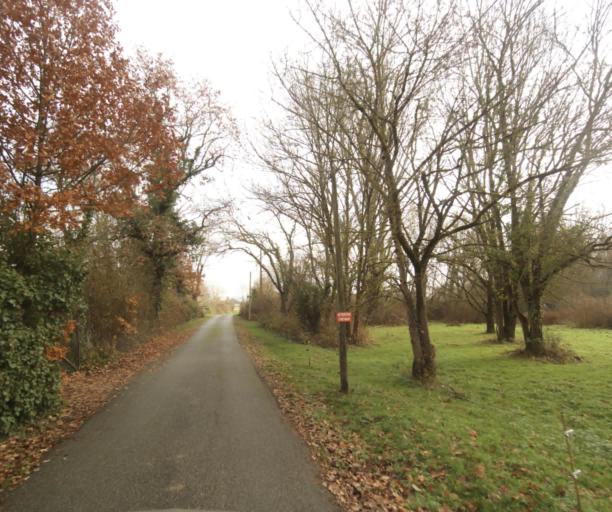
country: FR
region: Midi-Pyrenees
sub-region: Departement de la Haute-Garonne
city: Villemur-sur-Tarn
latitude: 43.8527
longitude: 1.4908
